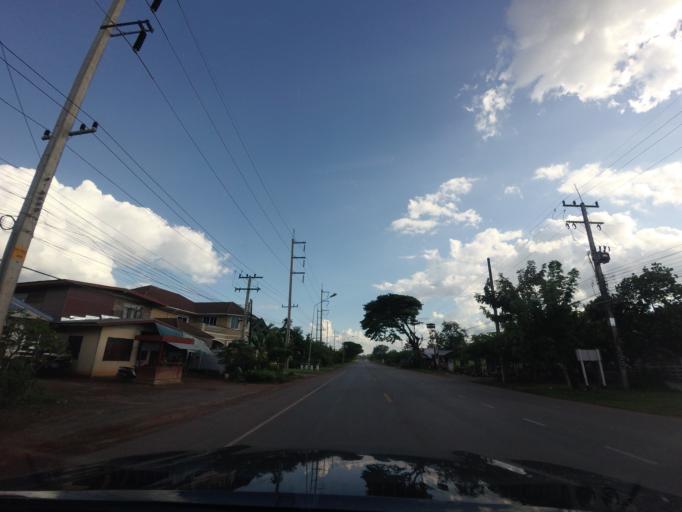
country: TH
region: Changwat Udon Thani
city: Thung Fon
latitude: 17.5073
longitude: 103.2034
